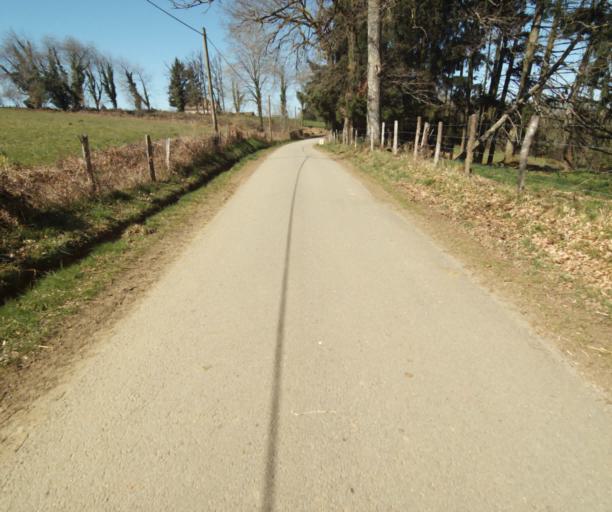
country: FR
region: Limousin
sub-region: Departement de la Correze
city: Saint-Clement
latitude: 45.3980
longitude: 1.6387
